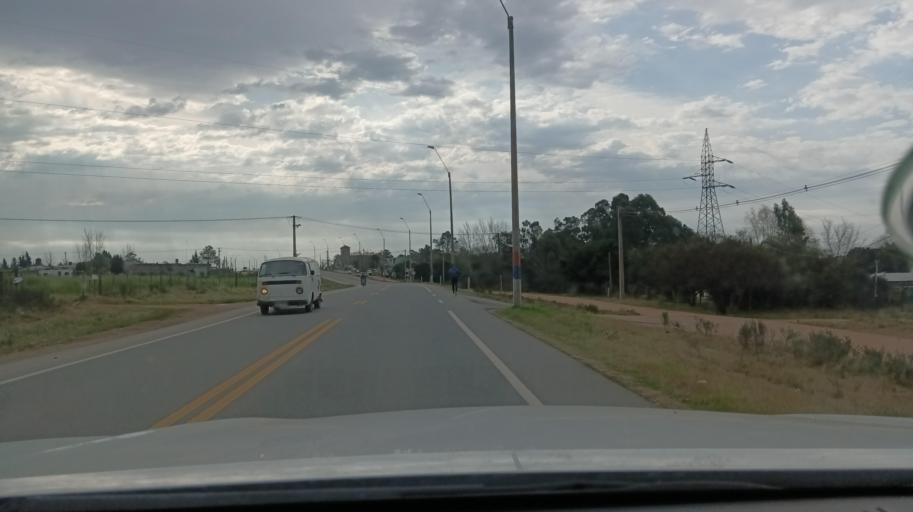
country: UY
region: Canelones
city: Toledo
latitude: -34.7428
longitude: -56.1121
